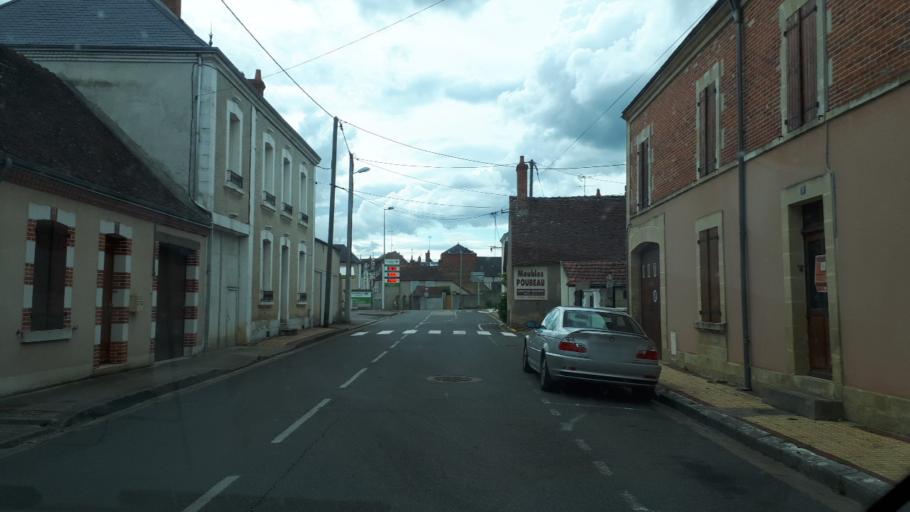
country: FR
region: Centre
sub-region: Departement du Cher
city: Gracay
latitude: 47.1439
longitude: 1.8491
